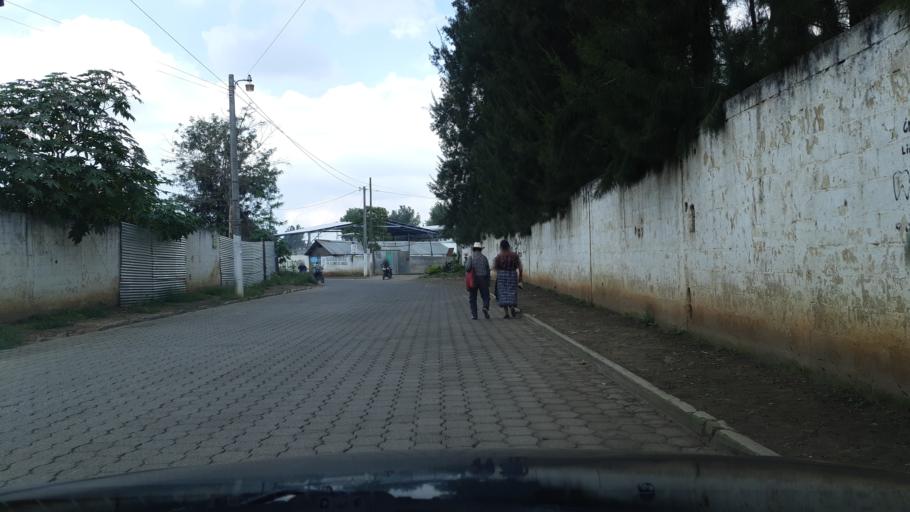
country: GT
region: Chimaltenango
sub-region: Municipio de Chimaltenango
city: Chimaltenango
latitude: 14.6699
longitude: -90.8092
